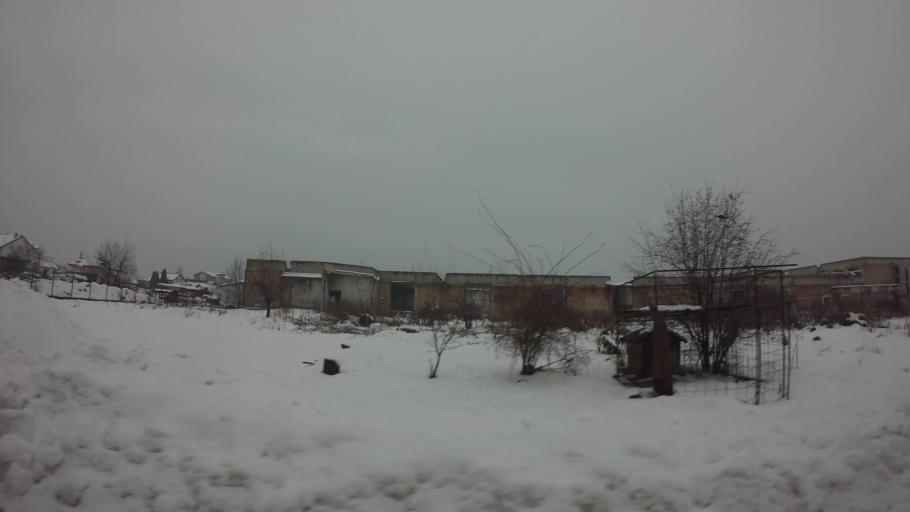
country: BA
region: Federation of Bosnia and Herzegovina
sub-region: Kanton Sarajevo
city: Sarajevo
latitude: 43.8434
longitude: 18.3120
